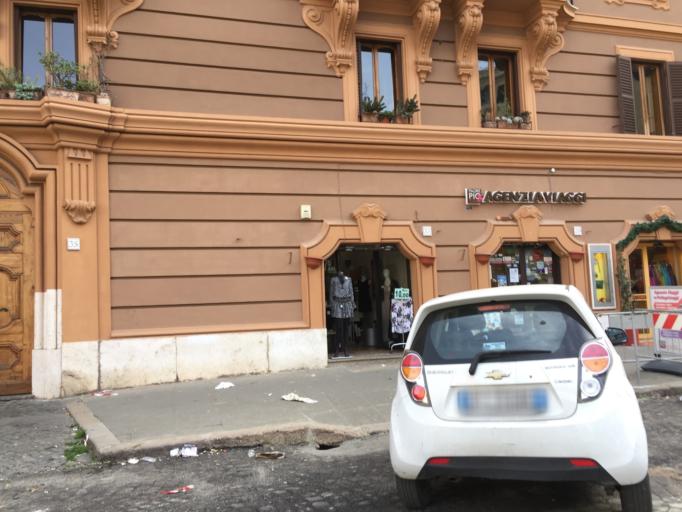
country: VA
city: Vatican City
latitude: 41.8987
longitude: 12.4554
